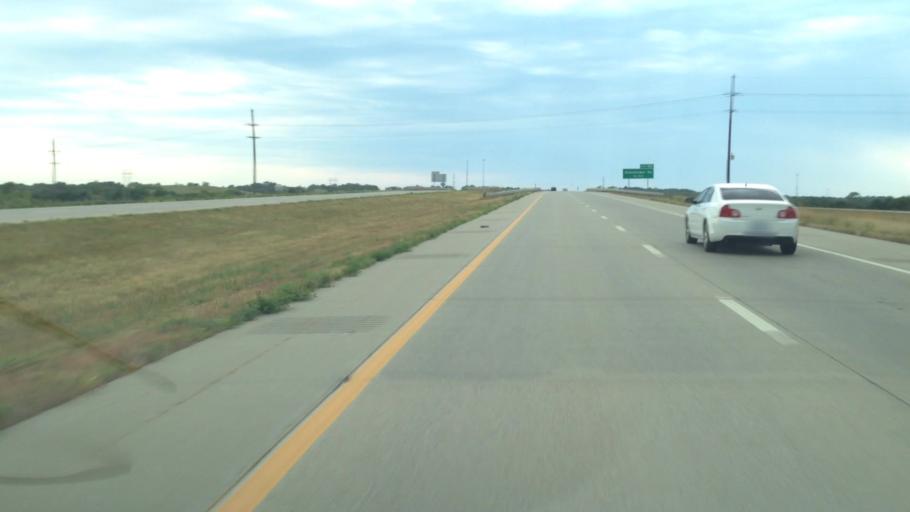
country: US
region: Kansas
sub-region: Franklin County
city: Ottawa
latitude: 38.5763
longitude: -95.2653
